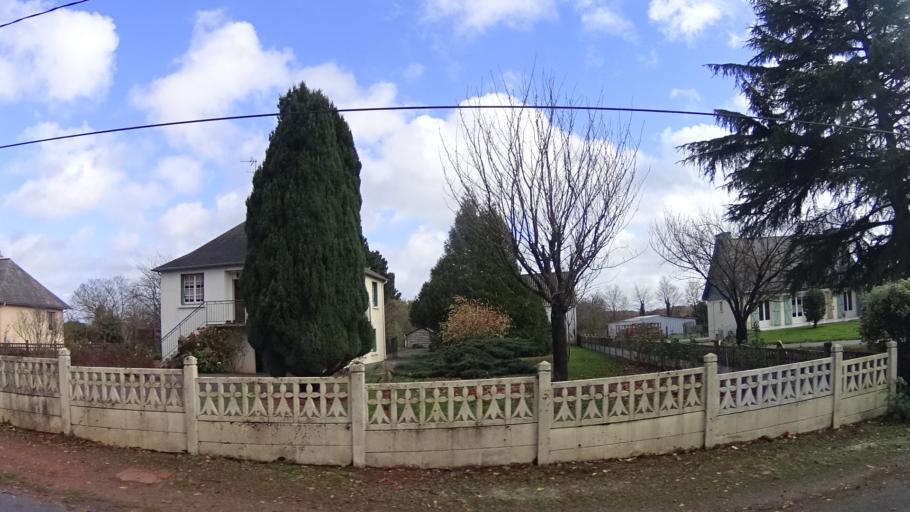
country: FR
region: Pays de la Loire
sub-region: Departement de la Loire-Atlantique
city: Saint-Nicolas-de-Redon
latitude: 47.6116
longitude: -2.0669
